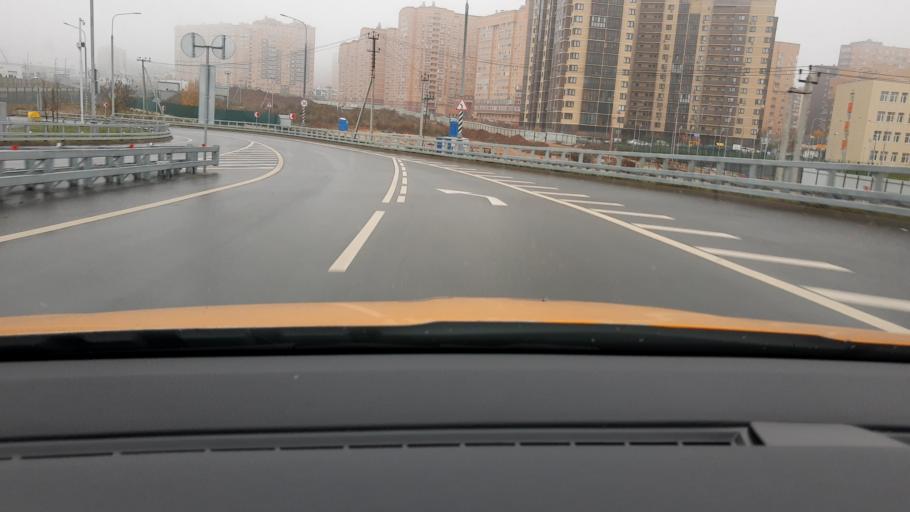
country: RU
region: Moskovskaya
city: Kommunarka
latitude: 55.5636
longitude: 37.4680
